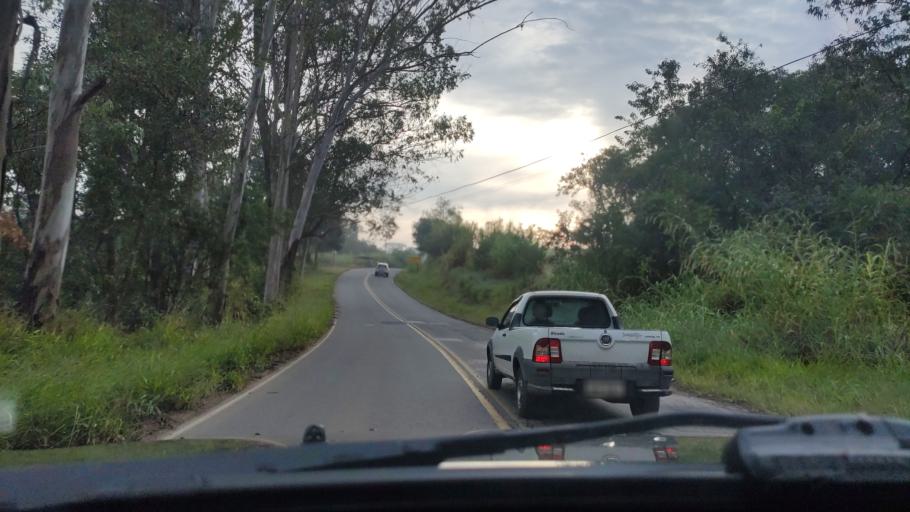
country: BR
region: Sao Paulo
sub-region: Campo Limpo Paulista
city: Campo Limpo Paulista
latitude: -23.1376
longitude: -46.7918
